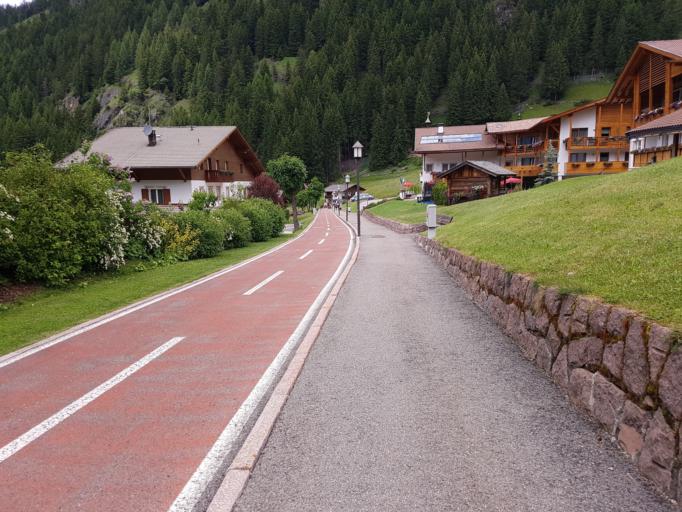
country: IT
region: Trentino-Alto Adige
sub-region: Bolzano
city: Selva
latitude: 46.5578
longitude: 11.7490
